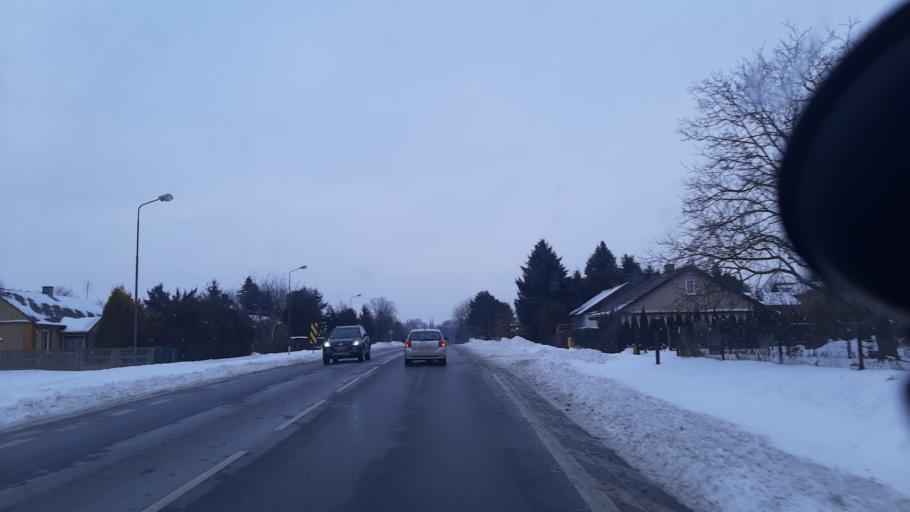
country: PL
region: Lublin Voivodeship
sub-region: Powiat lubelski
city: Garbow
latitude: 51.3577
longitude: 22.3203
